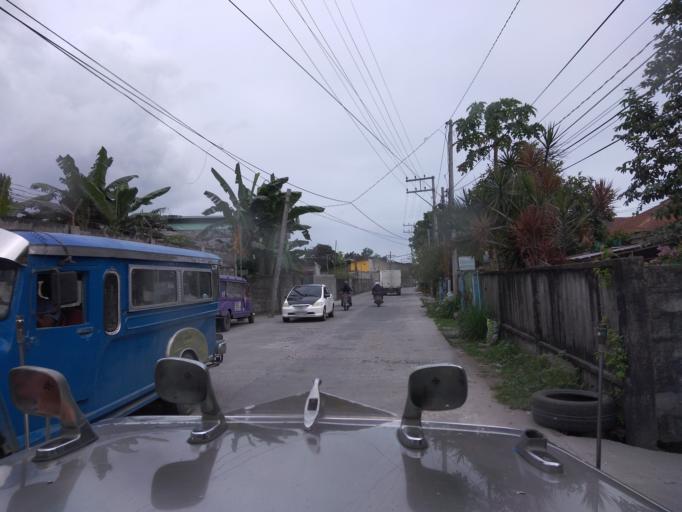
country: PH
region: Central Luzon
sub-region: Province of Pampanga
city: Pandacaqui
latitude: 15.1886
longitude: 120.6371
